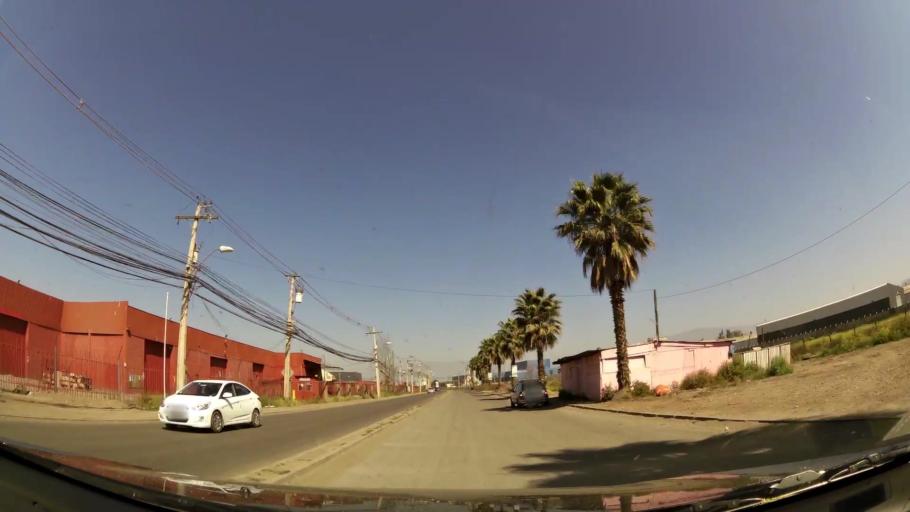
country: CL
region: Santiago Metropolitan
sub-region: Provincia de Chacabuco
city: Chicureo Abajo
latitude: -33.3138
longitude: -70.7248
